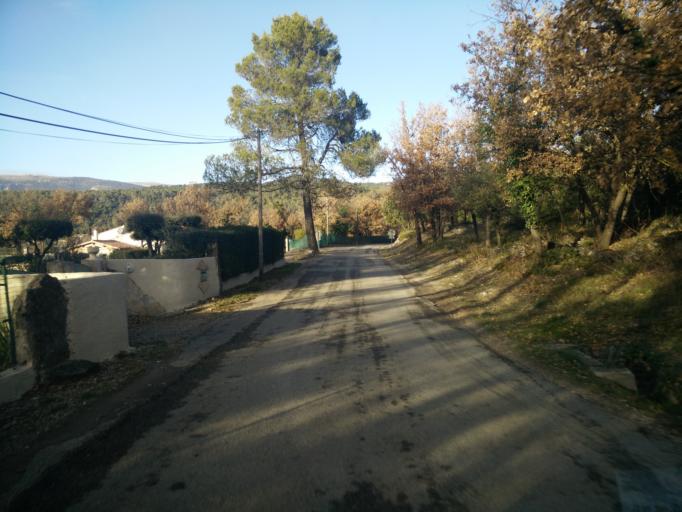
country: FR
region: Provence-Alpes-Cote d'Azur
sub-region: Departement du Var
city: Signes
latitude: 43.2817
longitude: 5.8436
